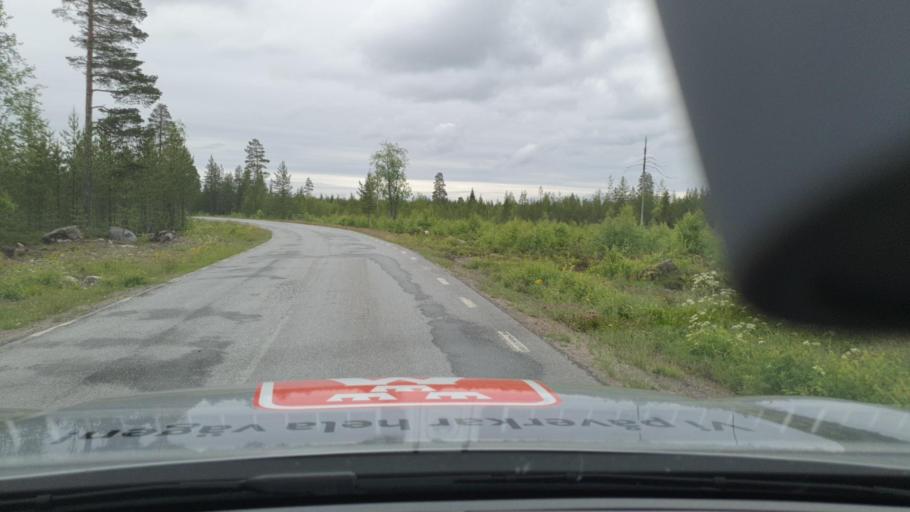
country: SE
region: Norrbotten
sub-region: Lulea Kommun
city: Ranea
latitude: 65.8343
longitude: 22.3085
